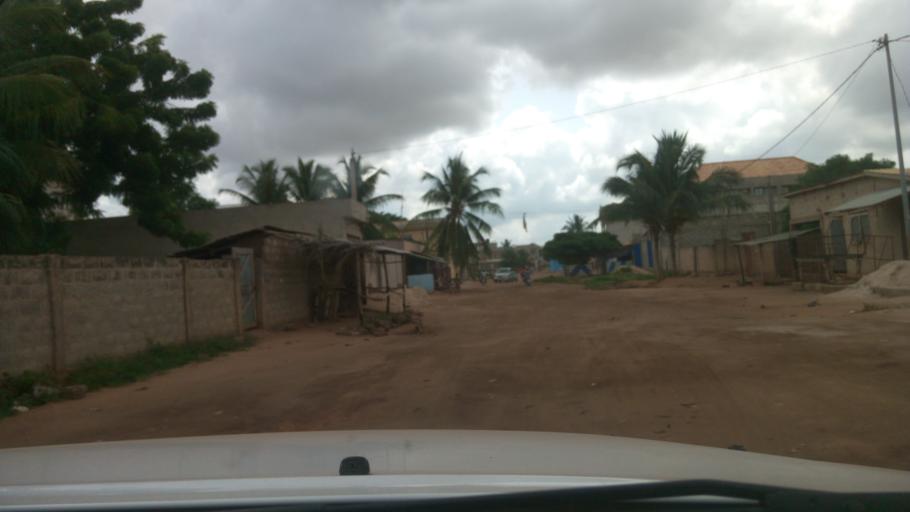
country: TG
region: Maritime
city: Lome
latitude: 6.2196
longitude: 1.1658
